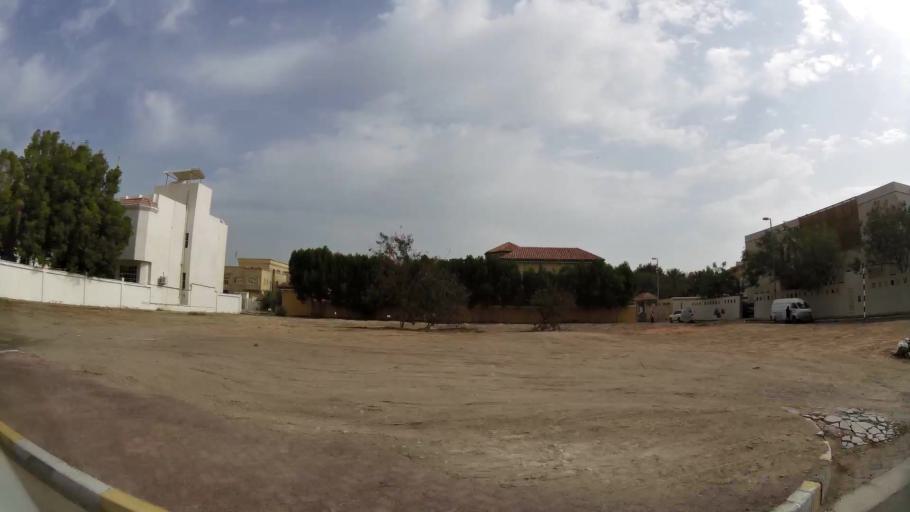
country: AE
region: Abu Dhabi
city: Abu Dhabi
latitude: 24.4526
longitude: 54.3735
